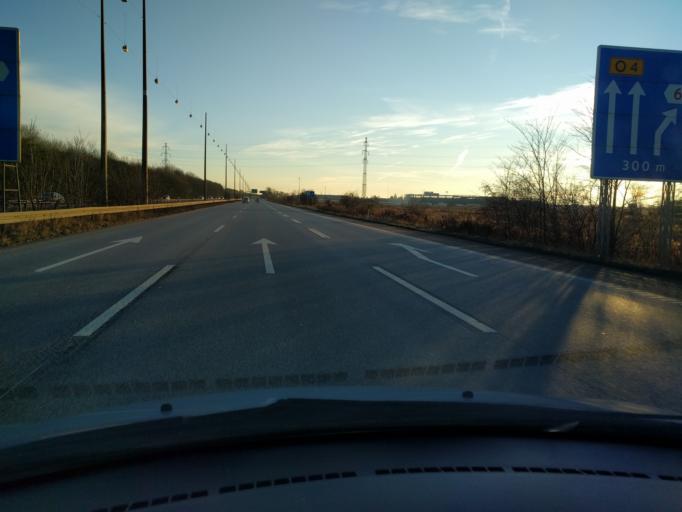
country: DK
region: Capital Region
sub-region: Ishoj Kommune
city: Ishoj
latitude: 55.6297
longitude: 12.3298
